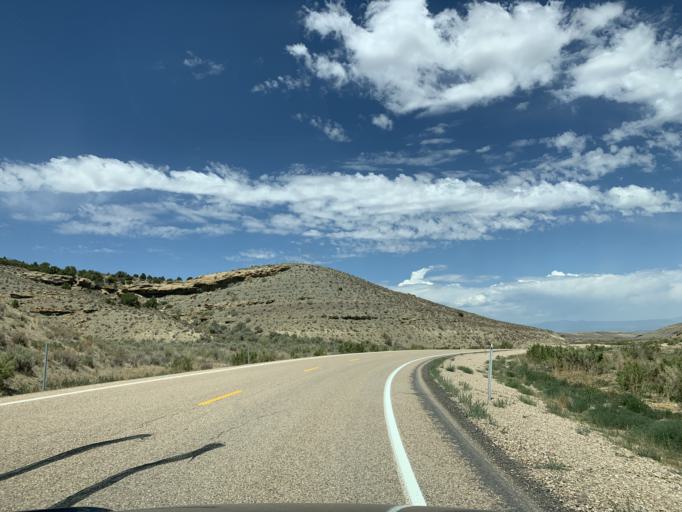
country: US
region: Utah
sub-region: Duchesne County
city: Duchesne
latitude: 40.0179
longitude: -110.1571
